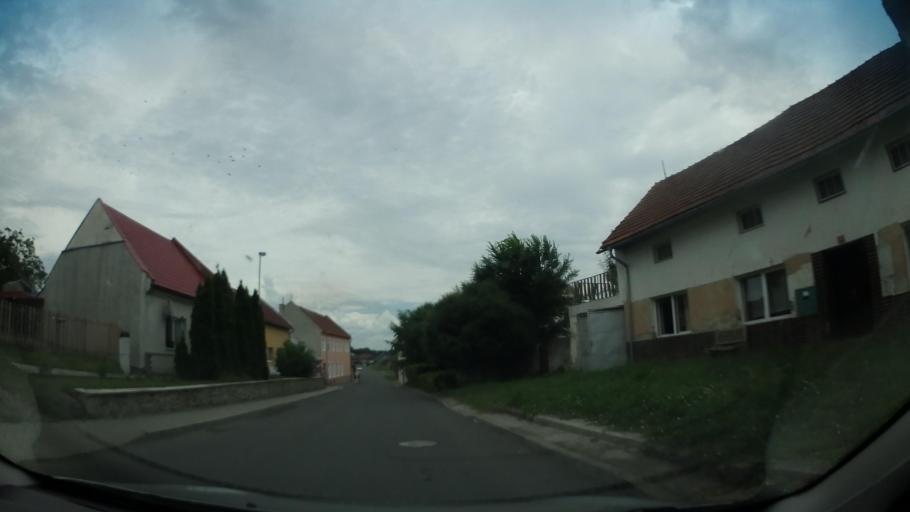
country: CZ
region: Olomoucky
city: Nezamyslice
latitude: 49.3276
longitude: 17.1427
